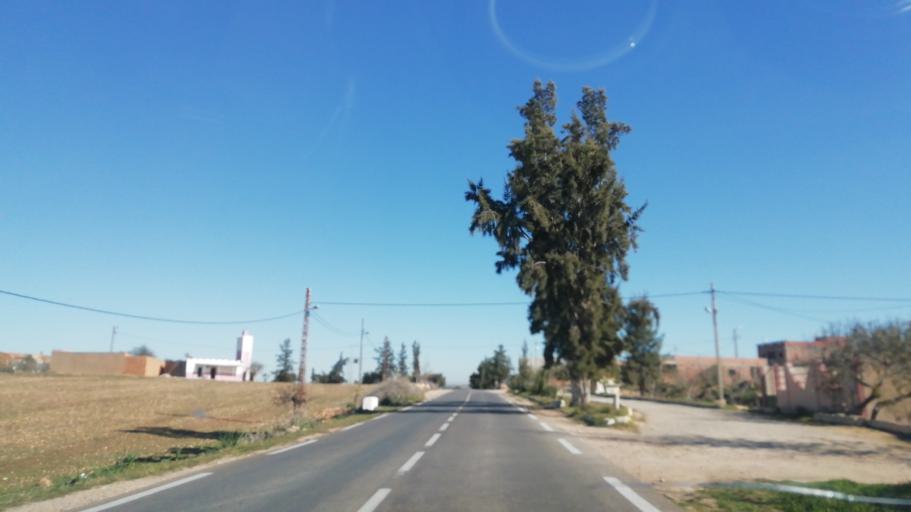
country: DZ
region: Tlemcen
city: Beni Mester
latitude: 34.8242
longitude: -1.6099
